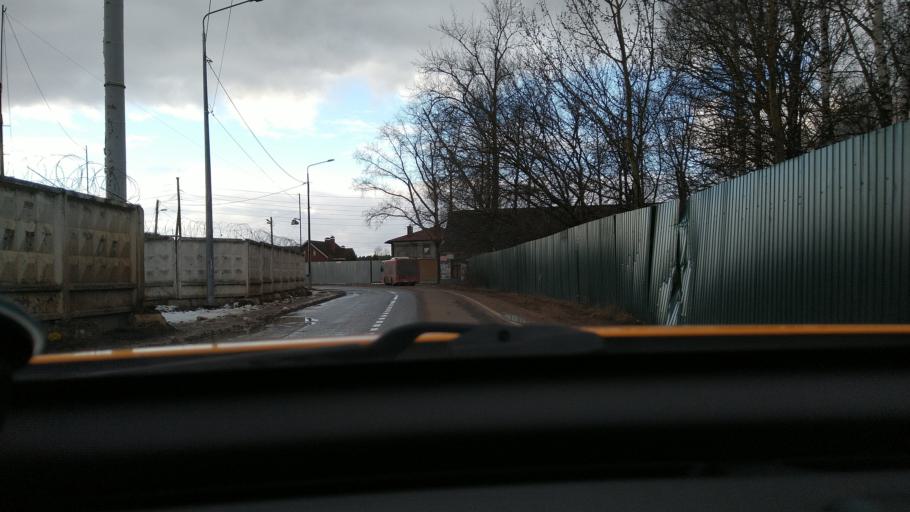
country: RU
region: Moskovskaya
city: Petrovo-Dal'neye
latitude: 55.7730
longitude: 37.2016
